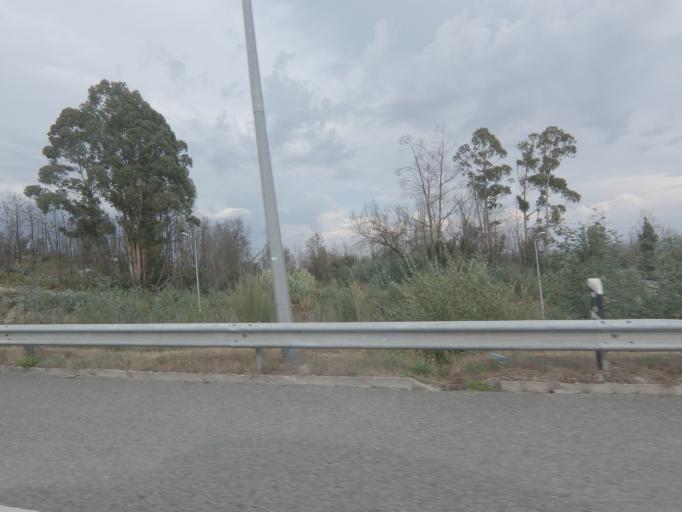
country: PT
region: Viseu
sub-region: Santa Comba Dao
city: Santa Comba Dao
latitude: 40.4380
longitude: -8.1096
